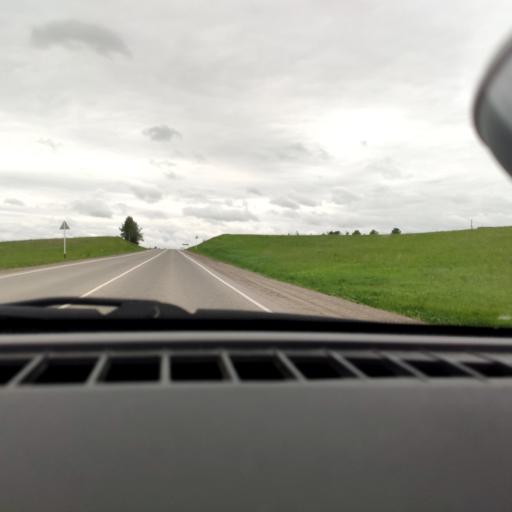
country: RU
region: Perm
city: Ust'-Kachka
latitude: 57.9011
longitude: 55.7845
